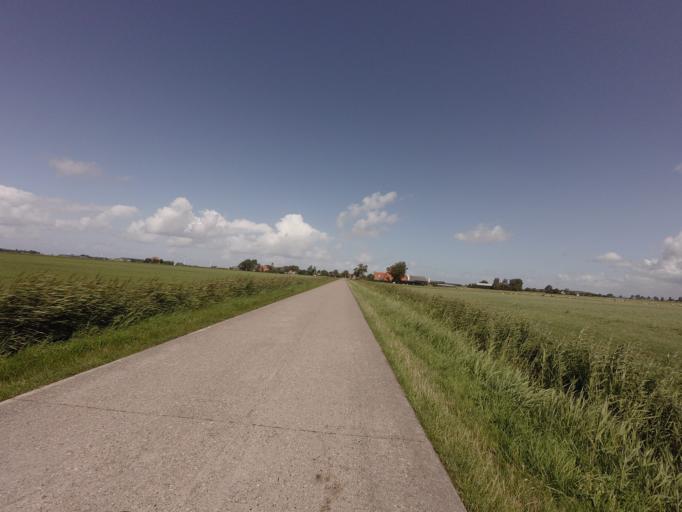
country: NL
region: Friesland
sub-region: Sudwest Fryslan
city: Makkum
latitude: 53.0742
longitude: 5.4533
